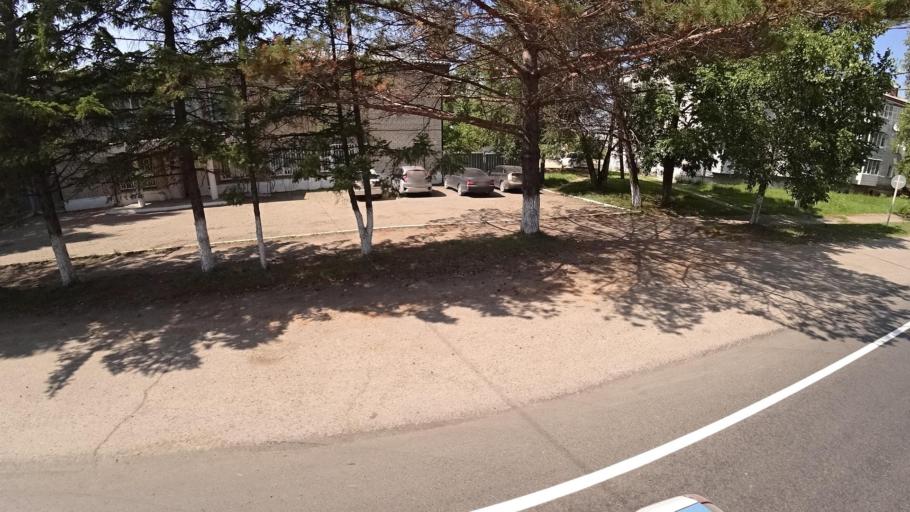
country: RU
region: Khabarovsk Krai
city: Khor
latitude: 47.9697
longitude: 135.0542
